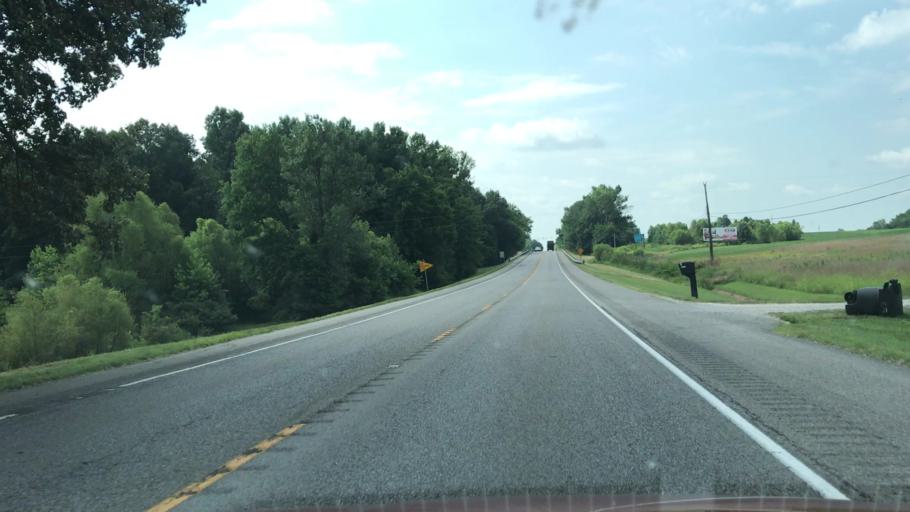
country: US
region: Kentucky
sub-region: Barren County
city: Glasgow
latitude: 37.0486
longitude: -85.9489
